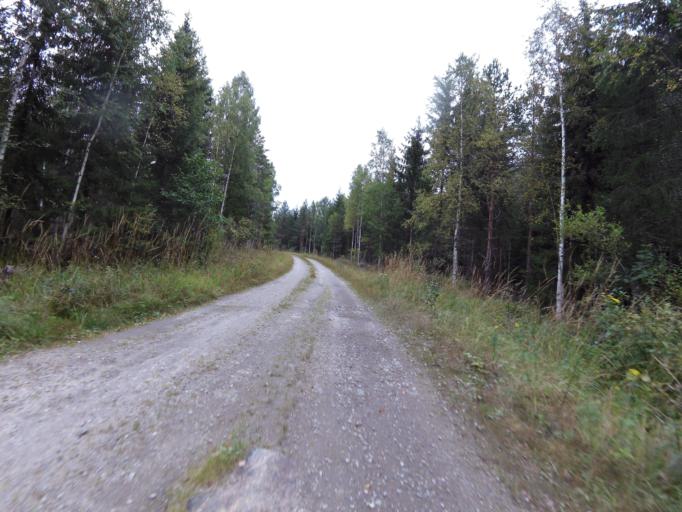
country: SE
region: Gaevleborg
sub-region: Gavle Kommun
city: Valbo
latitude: 60.7214
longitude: 17.0561
